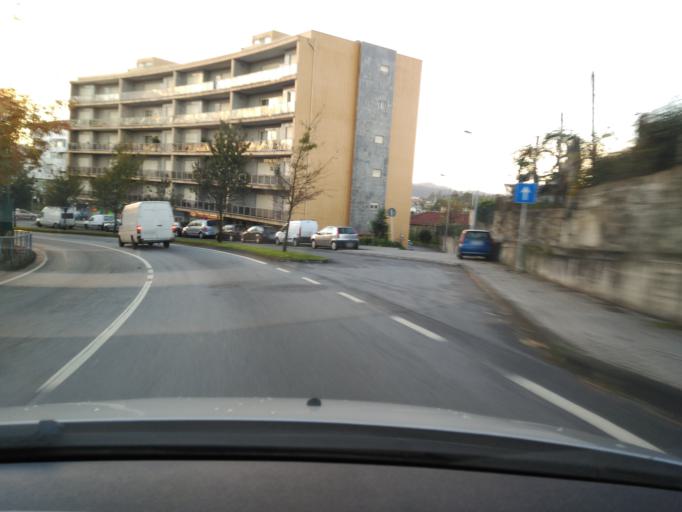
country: PT
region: Braga
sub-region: Guimaraes
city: Brito
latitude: 41.4836
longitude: -8.3533
